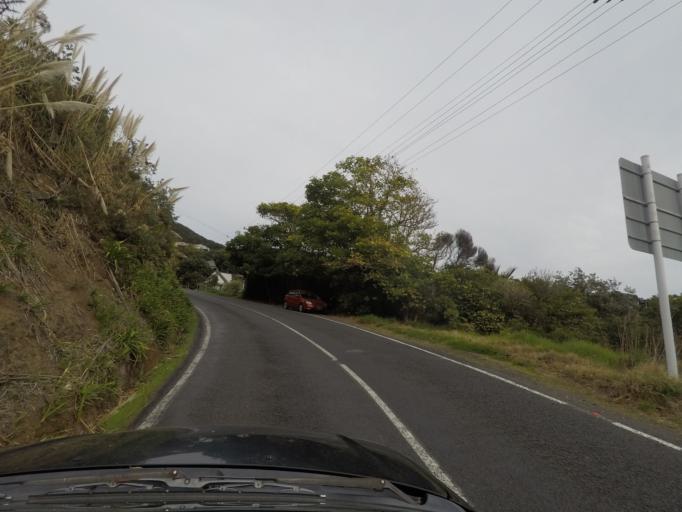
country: NZ
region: Auckland
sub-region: Auckland
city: Muriwai Beach
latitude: -36.9548
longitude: 174.4743
